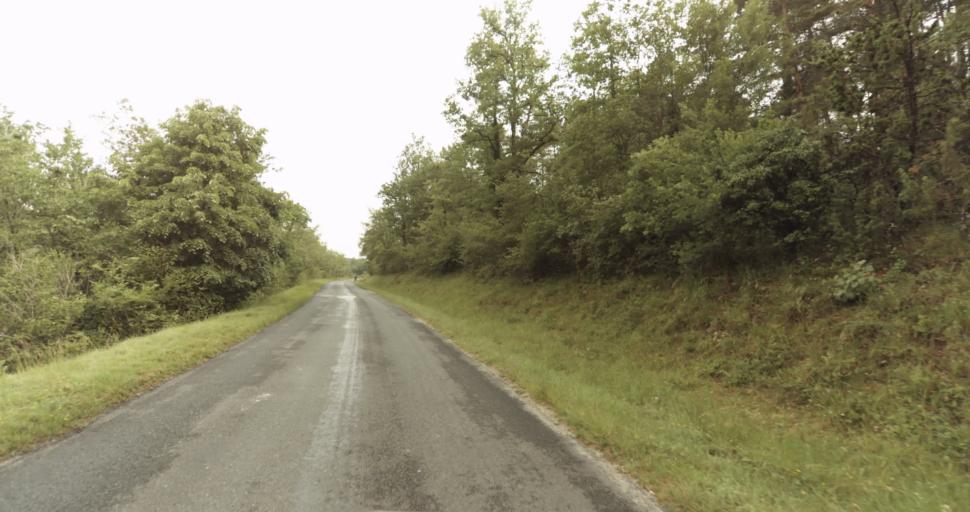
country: FR
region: Aquitaine
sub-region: Departement de la Dordogne
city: Lalinde
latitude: 44.8901
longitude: 0.7724
